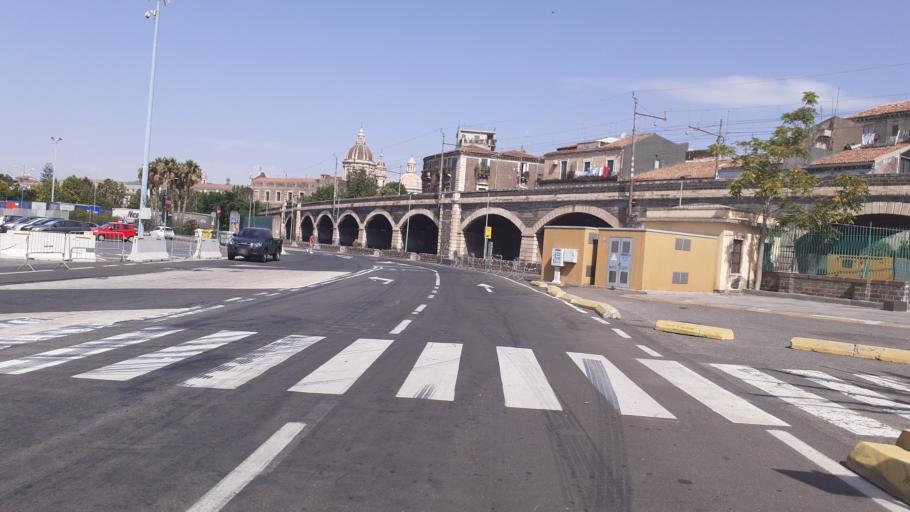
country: IT
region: Sicily
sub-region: Catania
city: Catania
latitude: 37.5007
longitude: 15.0924
